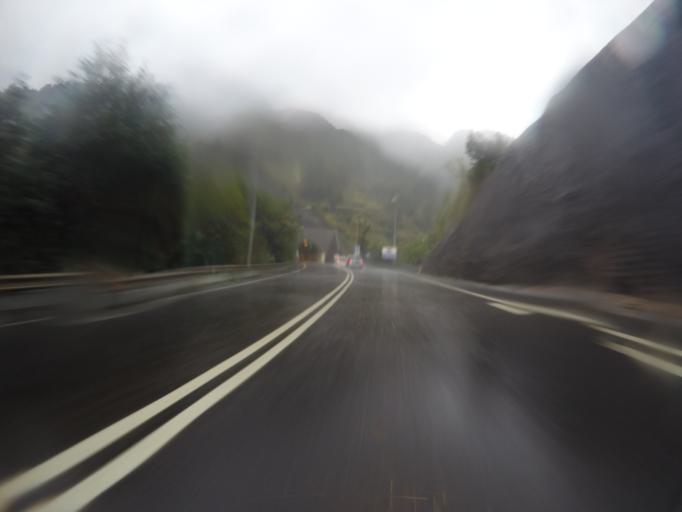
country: PT
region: Madeira
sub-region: Santa Cruz
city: Santa Cruz
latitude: 32.7532
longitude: -16.8190
